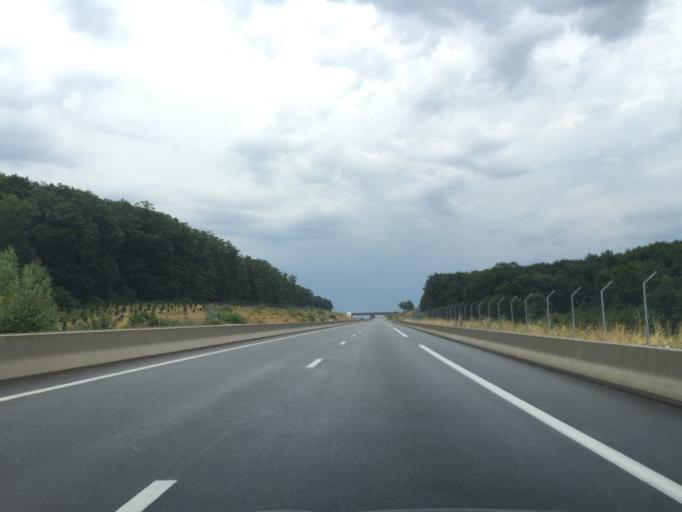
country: FR
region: Auvergne
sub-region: Departement de l'Allier
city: Lapalisse
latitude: 46.2192
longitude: 3.6931
